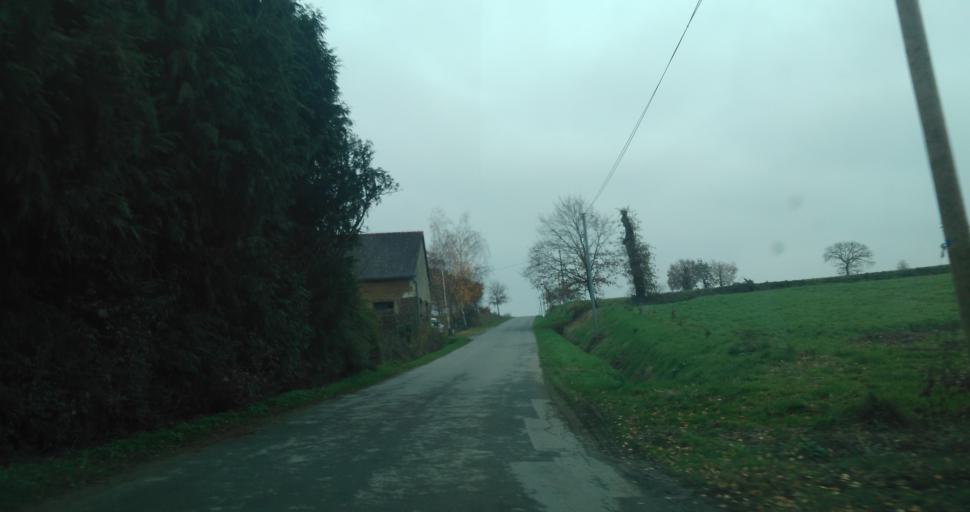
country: FR
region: Brittany
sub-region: Departement d'Ille-et-Vilaine
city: Iffendic
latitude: 48.0946
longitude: -2.0922
